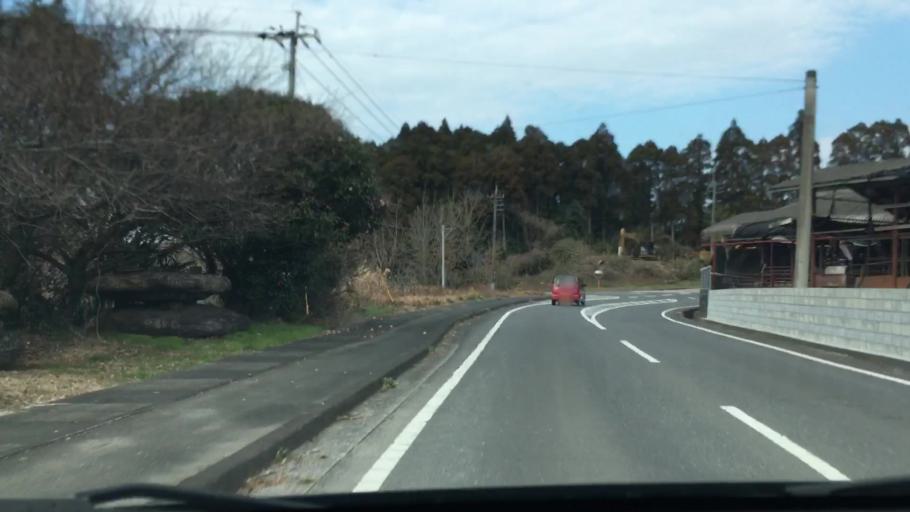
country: JP
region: Miyazaki
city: Kushima
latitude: 31.5036
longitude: 131.2390
